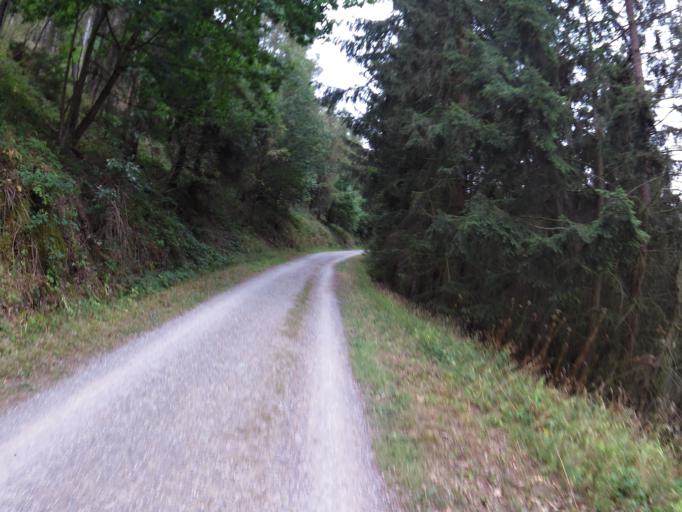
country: DE
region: North Rhine-Westphalia
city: Heimbach
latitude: 50.6331
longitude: 6.4225
